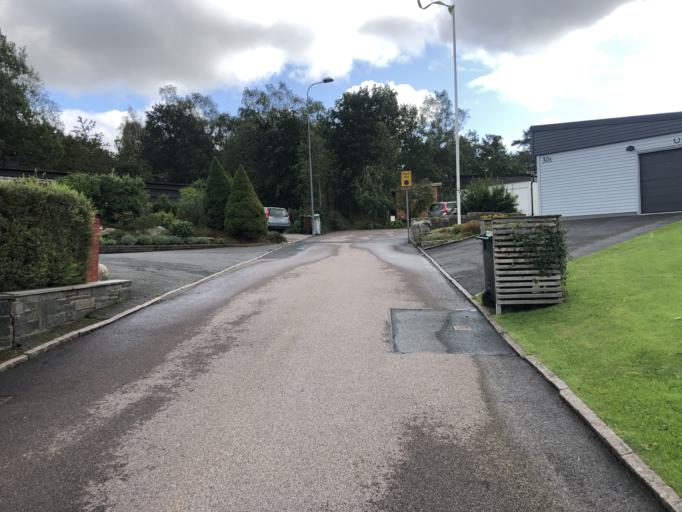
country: SE
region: Vaestra Goetaland
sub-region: Goteborg
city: Goeteborg
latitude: 57.7566
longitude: 11.9302
